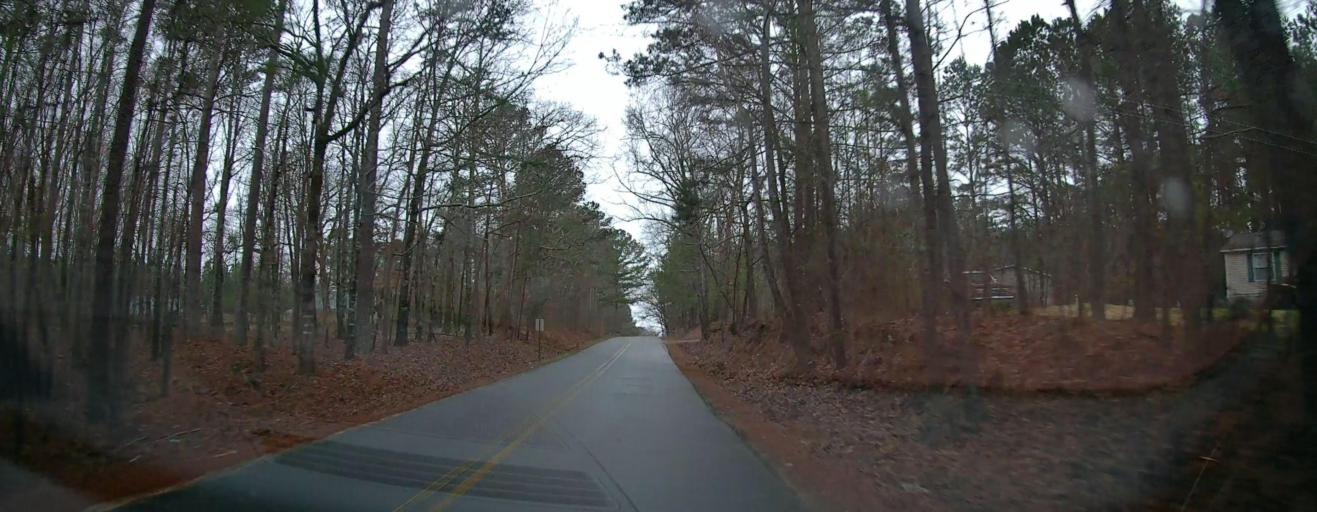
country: US
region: Georgia
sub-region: Monroe County
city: Forsyth
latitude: 33.0872
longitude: -83.9307
